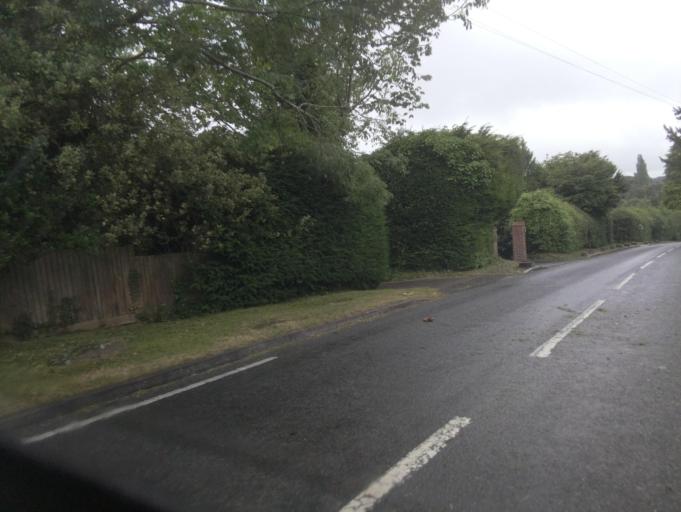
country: GB
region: England
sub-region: Surrey
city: Reigate
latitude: 51.2487
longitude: -0.1960
